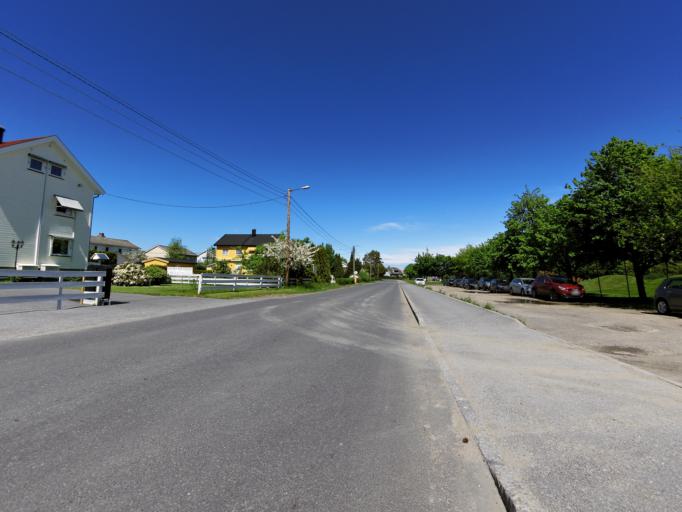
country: NO
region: Ostfold
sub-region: Fredrikstad
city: Fredrikstad
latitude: 59.2309
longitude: 10.9714
